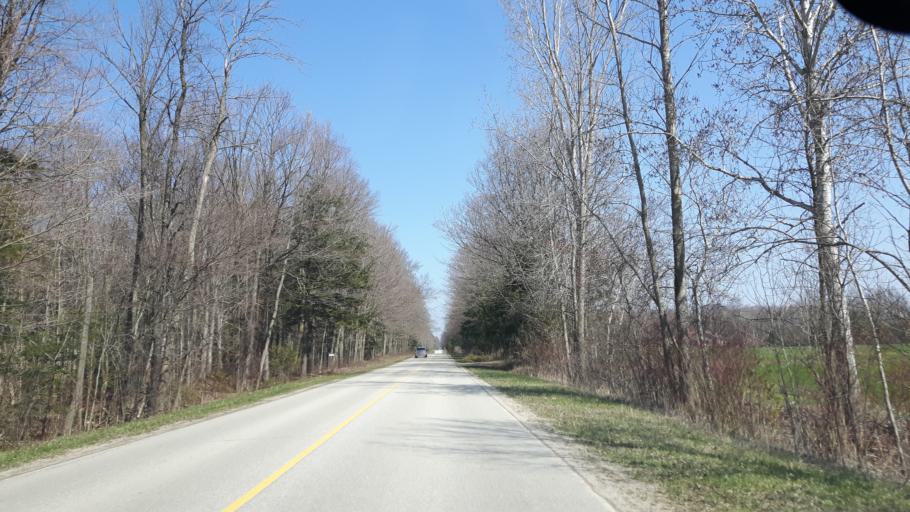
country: CA
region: Ontario
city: Bluewater
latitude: 43.5931
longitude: -81.6848
